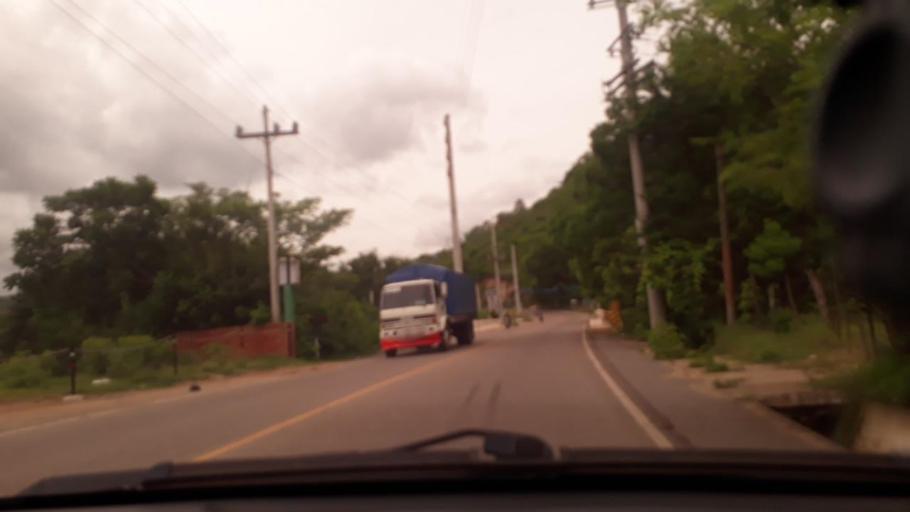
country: GT
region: Chiquimula
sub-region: Municipio de Jocotan
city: Jocotan
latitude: 14.8165
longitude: -89.3820
